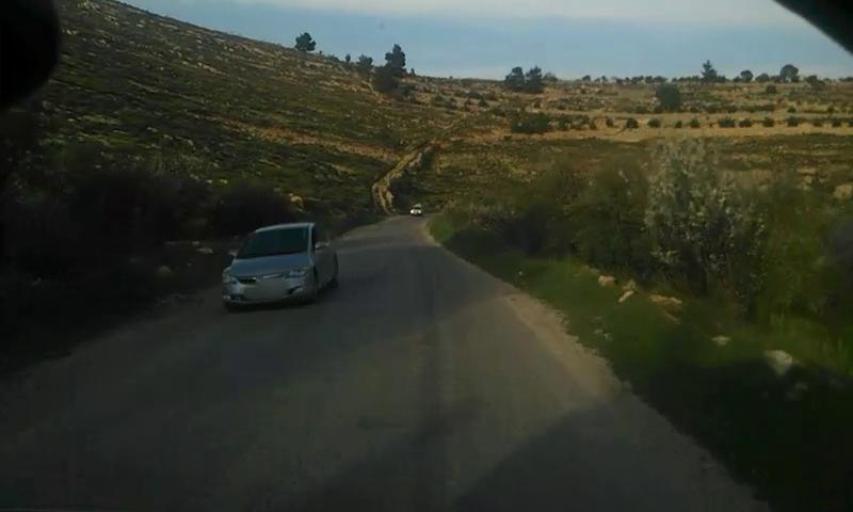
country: PS
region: West Bank
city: Ash Shuyukh
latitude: 31.5960
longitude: 35.1730
